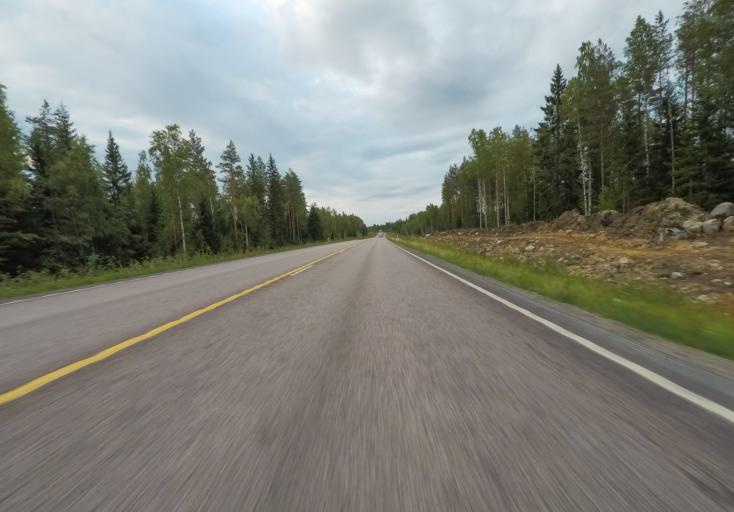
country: FI
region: Central Finland
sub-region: Joutsa
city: Leivonmaeki
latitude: 61.8471
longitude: 26.0995
